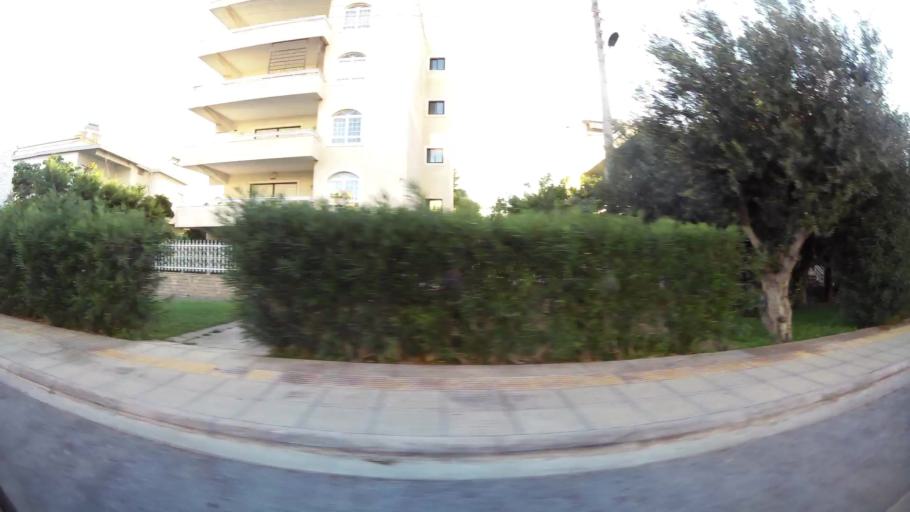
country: GR
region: Attica
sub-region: Nomarchia Athinas
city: Glyfada
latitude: 37.8678
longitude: 23.7553
